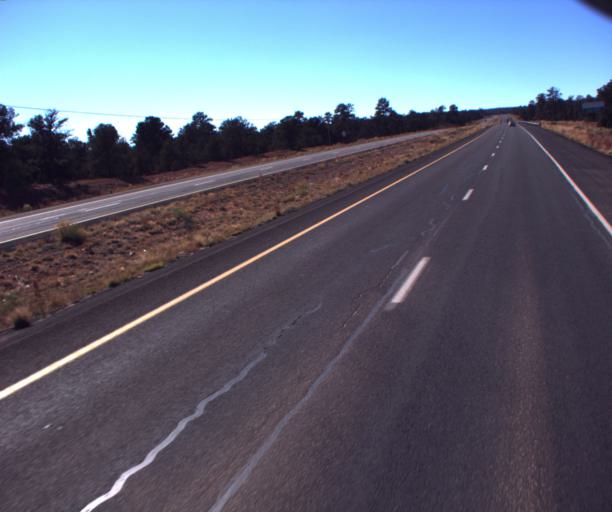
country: US
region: Arizona
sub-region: Apache County
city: Saint Michaels
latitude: 35.6593
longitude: -109.1253
